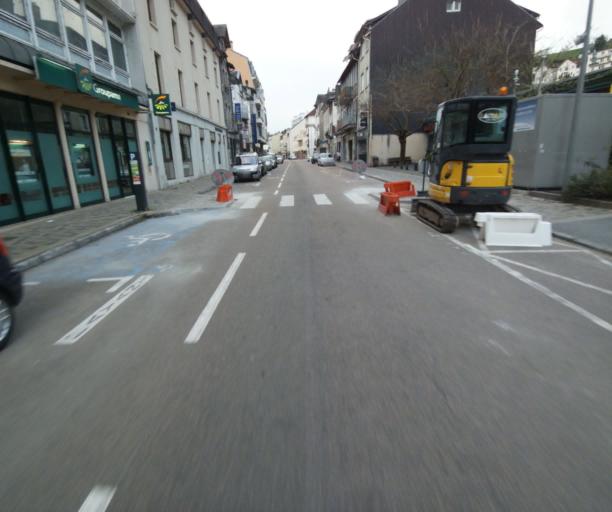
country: FR
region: Limousin
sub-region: Departement de la Correze
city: Tulle
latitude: 45.2636
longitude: 1.7640
